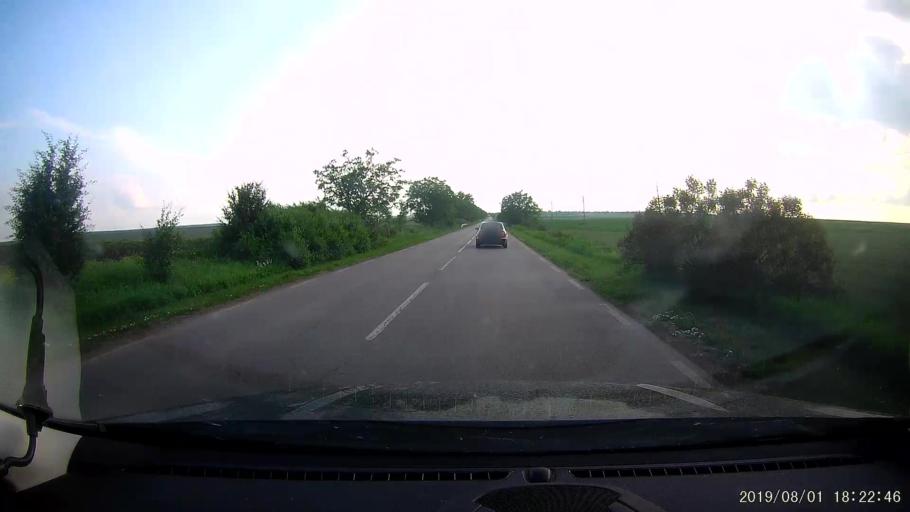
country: BG
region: Shumen
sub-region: Obshtina Kaolinovo
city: Kaolinovo
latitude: 43.6380
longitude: 27.0425
